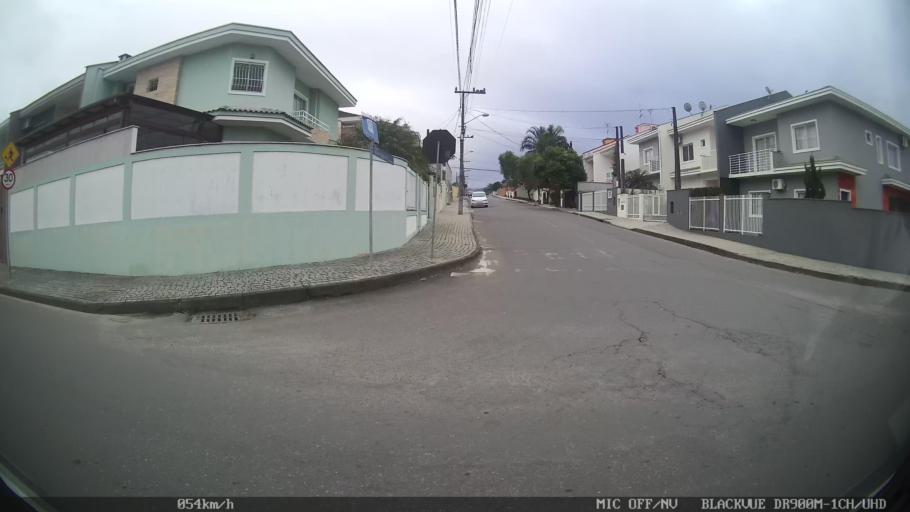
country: BR
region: Santa Catarina
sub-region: Joinville
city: Joinville
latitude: -26.2774
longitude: -48.8783
